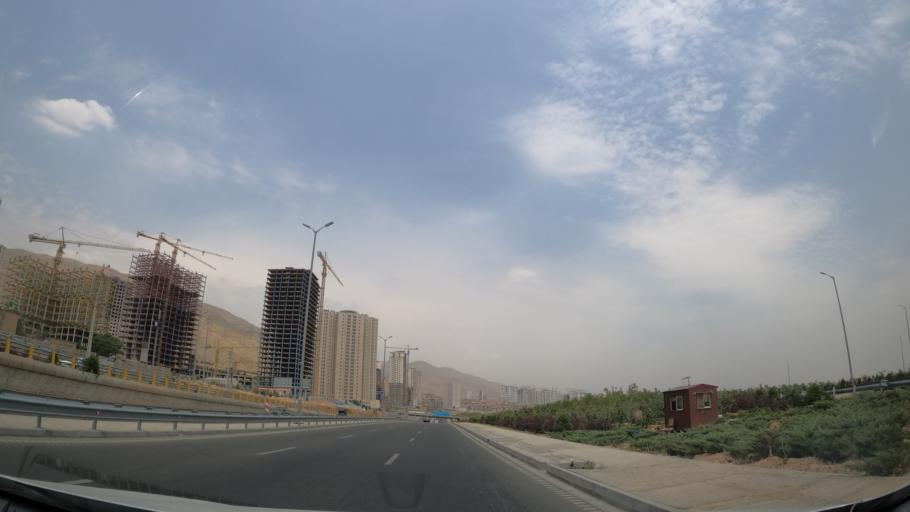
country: IR
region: Tehran
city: Shahr-e Qods
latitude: 35.7489
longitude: 51.1323
